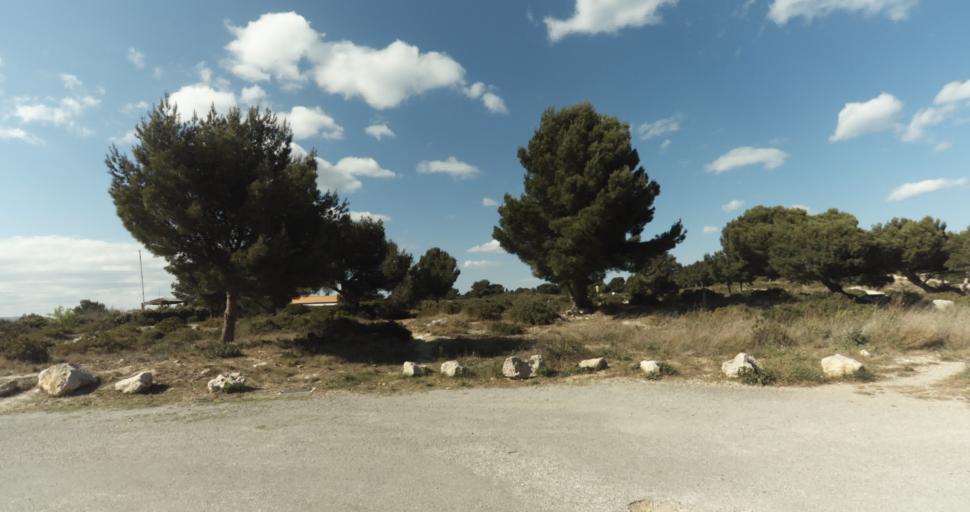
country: FR
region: Languedoc-Roussillon
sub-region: Departement de l'Aude
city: Leucate
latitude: 42.9073
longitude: 3.0548
